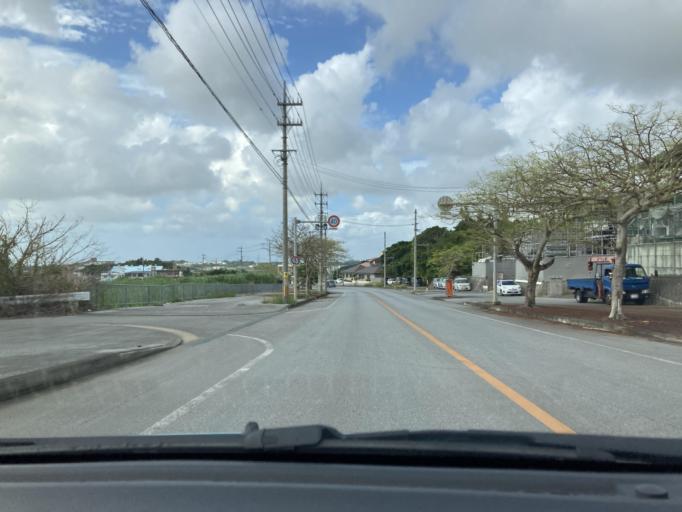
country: JP
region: Okinawa
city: Itoman
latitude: 26.1234
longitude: 127.6933
